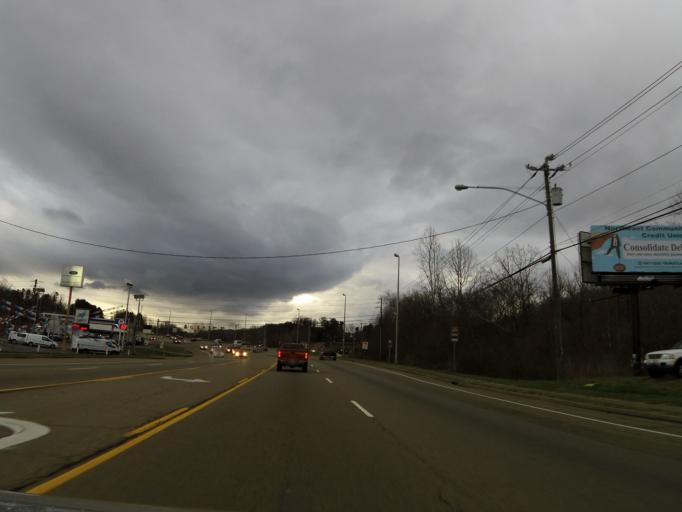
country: US
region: Tennessee
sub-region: Carter County
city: Central
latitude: 36.3304
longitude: -82.2685
